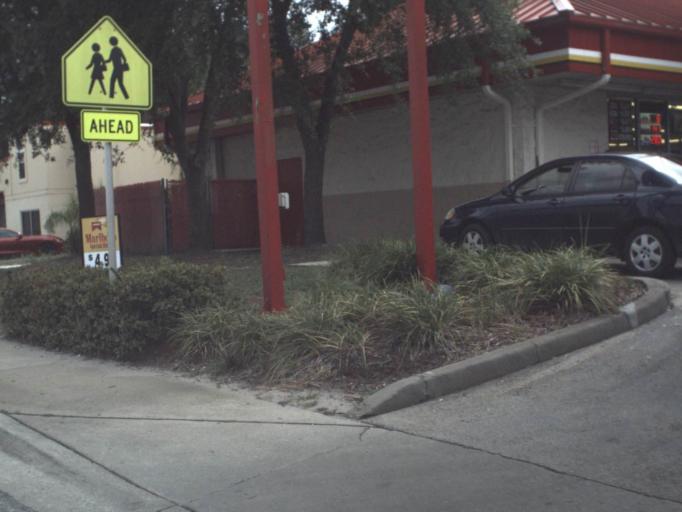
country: US
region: Florida
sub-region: Bradford County
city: Starke
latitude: 29.9510
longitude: -82.1092
